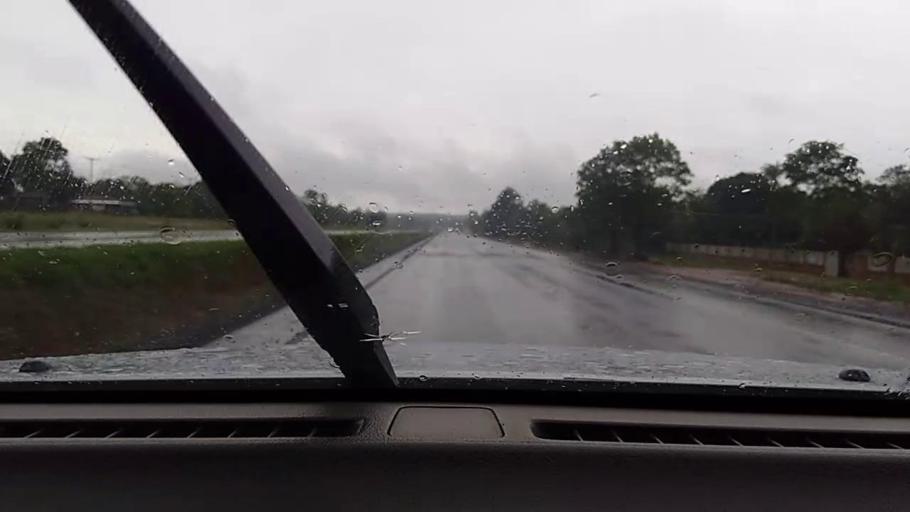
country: PY
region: Caaguazu
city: Repatriacion
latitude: -25.4626
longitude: -55.9275
